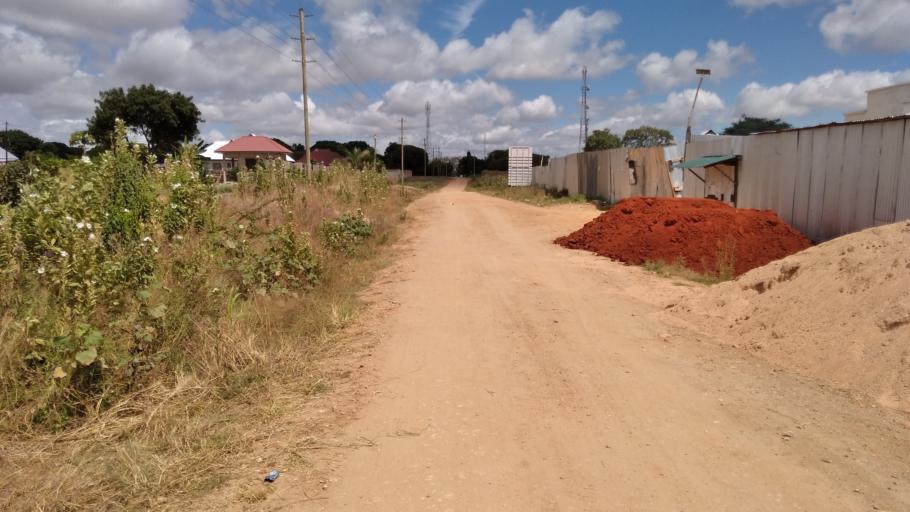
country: TZ
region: Dodoma
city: Dodoma
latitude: -6.1891
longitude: 35.7563
